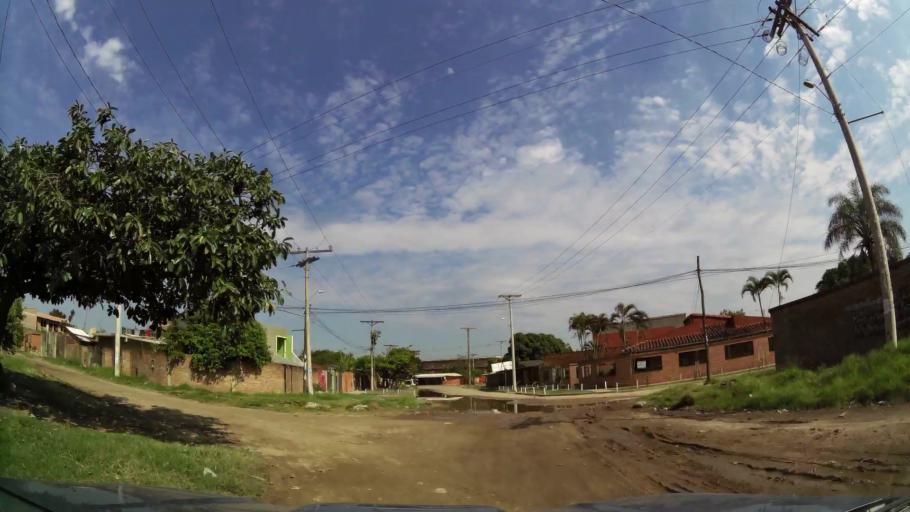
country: BO
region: Santa Cruz
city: Santa Cruz de la Sierra
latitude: -17.7251
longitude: -63.1544
